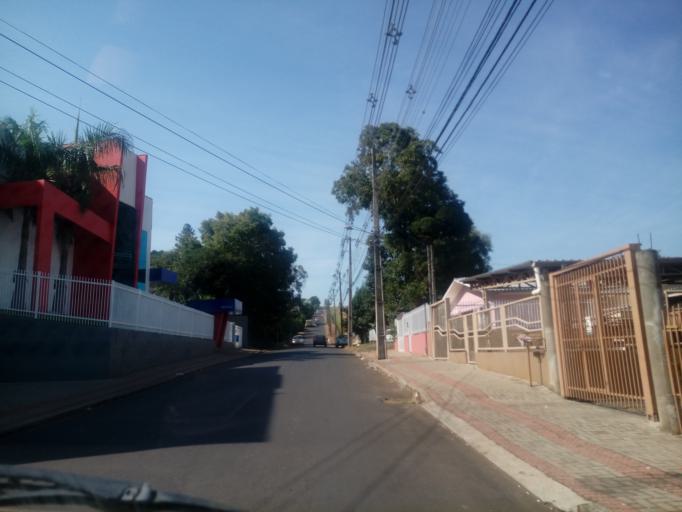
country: BR
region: Santa Catarina
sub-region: Chapeco
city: Chapeco
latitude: -27.0802
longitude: -52.6392
